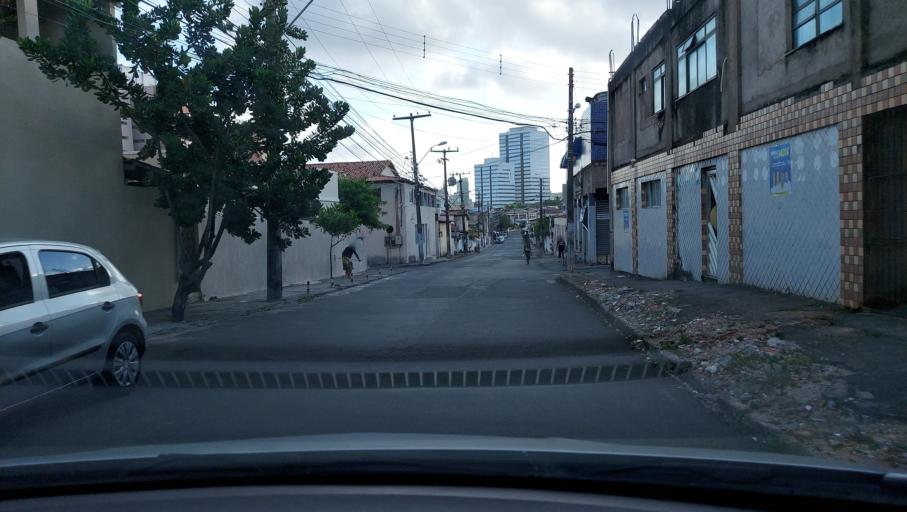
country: BR
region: Bahia
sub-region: Salvador
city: Salvador
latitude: -12.9857
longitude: -38.4446
